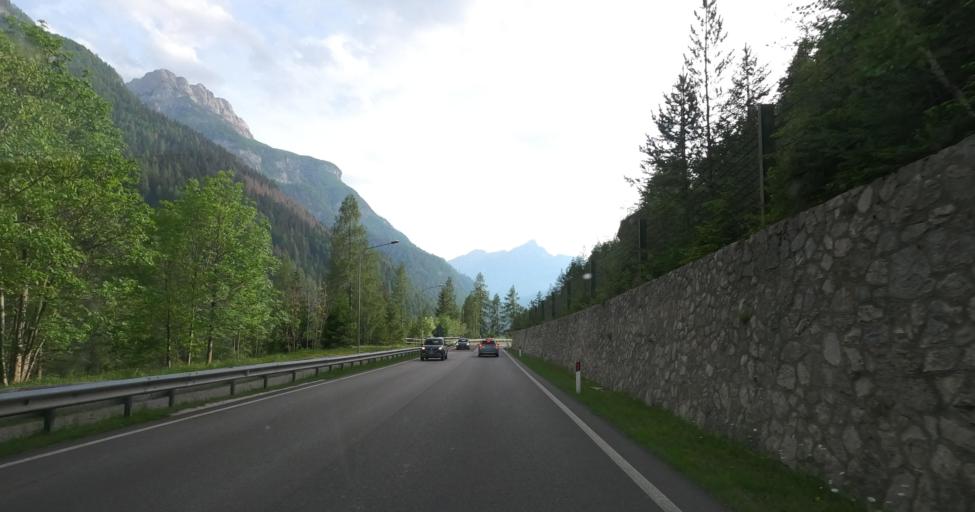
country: IT
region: Veneto
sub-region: Provincia di Belluno
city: Alleghe
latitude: 46.3962
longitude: 12.0105
